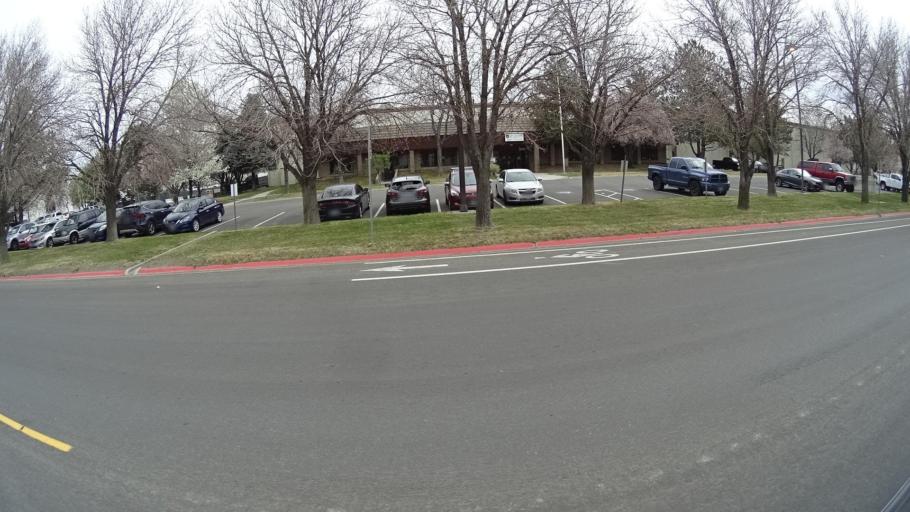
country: US
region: Nevada
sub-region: Washoe County
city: Sparks
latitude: 39.5203
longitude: -119.7369
